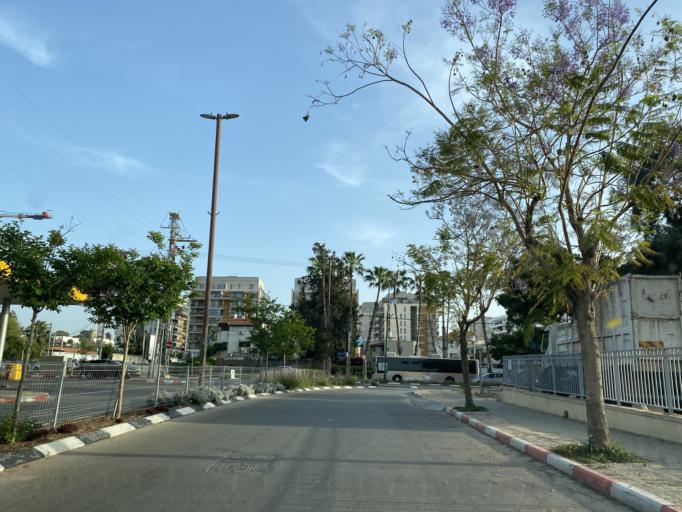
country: IL
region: Tel Aviv
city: Herzliyya
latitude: 32.1636
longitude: 34.8301
